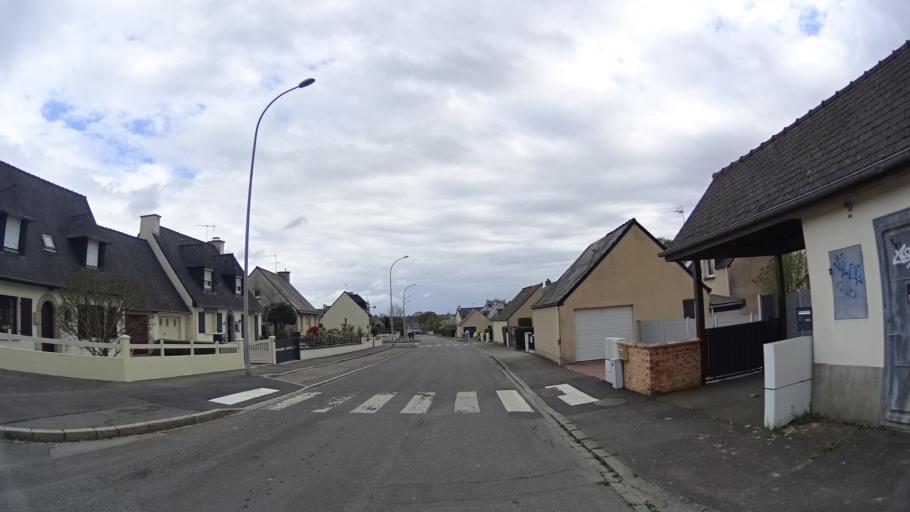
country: FR
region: Brittany
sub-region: Departement d'Ille-et-Vilaine
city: Le Rheu
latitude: 48.1248
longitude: -1.8101
